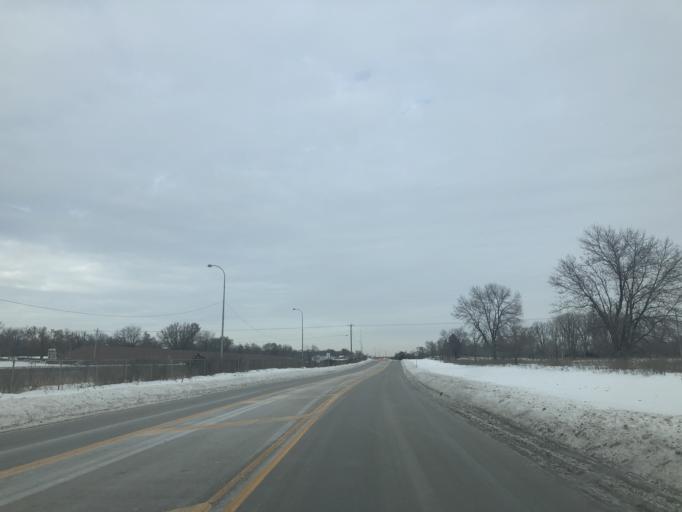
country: US
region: Minnesota
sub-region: Ramsey County
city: Mounds View
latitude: 45.0992
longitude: -93.1876
